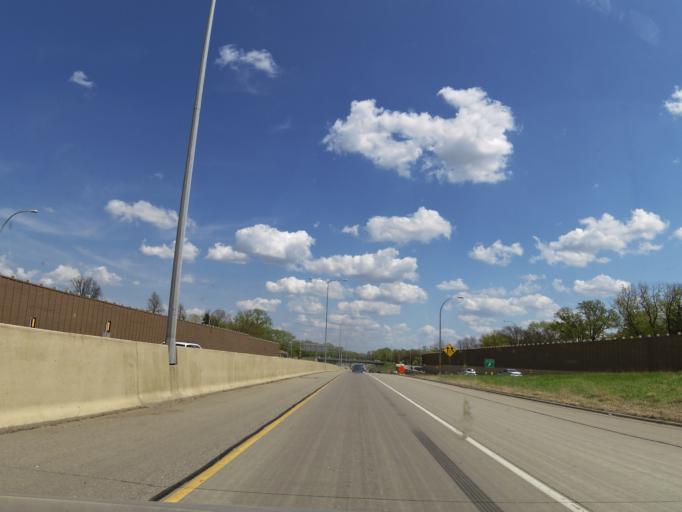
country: US
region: Minnesota
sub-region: Hennepin County
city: Richfield
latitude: 44.8906
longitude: -93.2723
